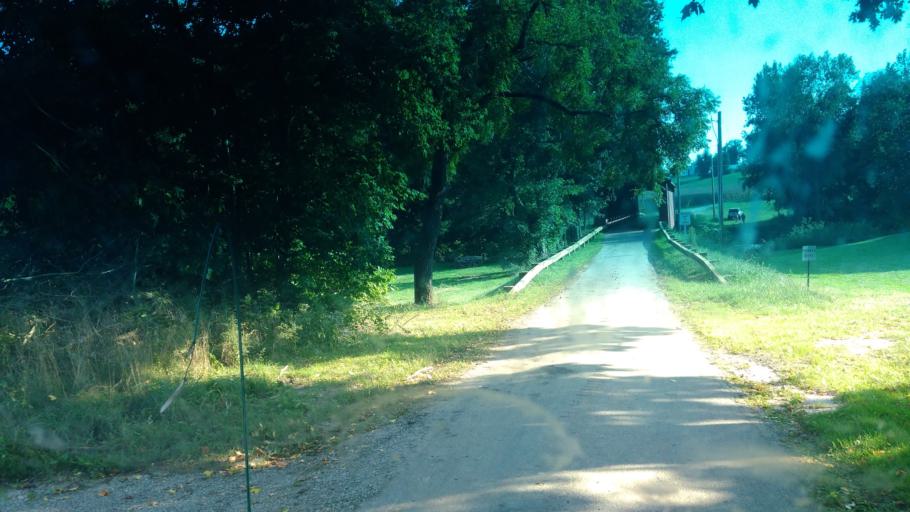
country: US
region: Ohio
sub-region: Wyandot County
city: Upper Sandusky
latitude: 40.9038
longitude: -83.2444
